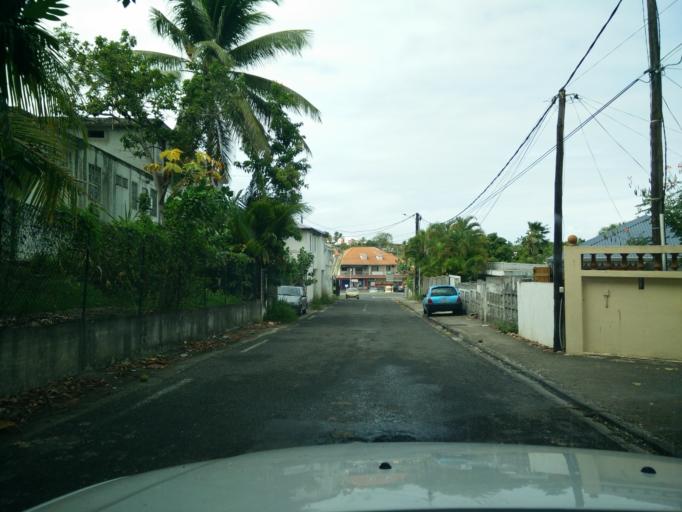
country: GP
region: Guadeloupe
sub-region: Guadeloupe
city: Le Gosier
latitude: 16.2092
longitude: -61.4656
